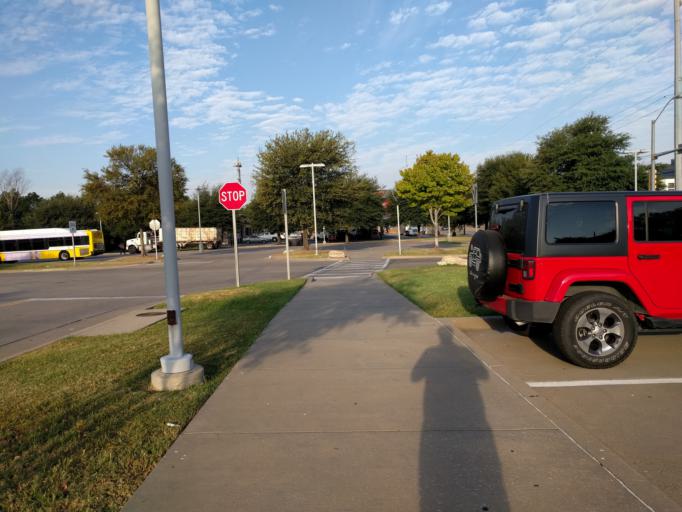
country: US
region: Texas
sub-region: Dallas County
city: Richardson
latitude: 32.9089
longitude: -96.7629
